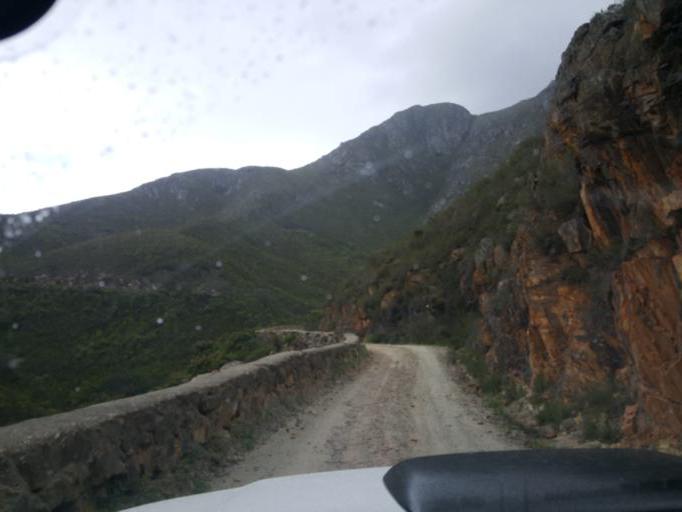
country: ZA
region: Western Cape
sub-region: Eden District Municipality
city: George
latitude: -33.8915
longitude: 22.4258
